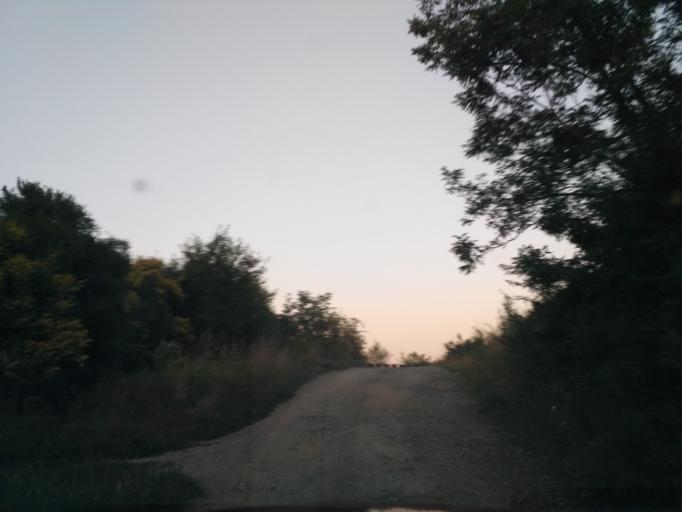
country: SK
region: Kosicky
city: Kosice
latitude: 48.7240
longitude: 21.2198
